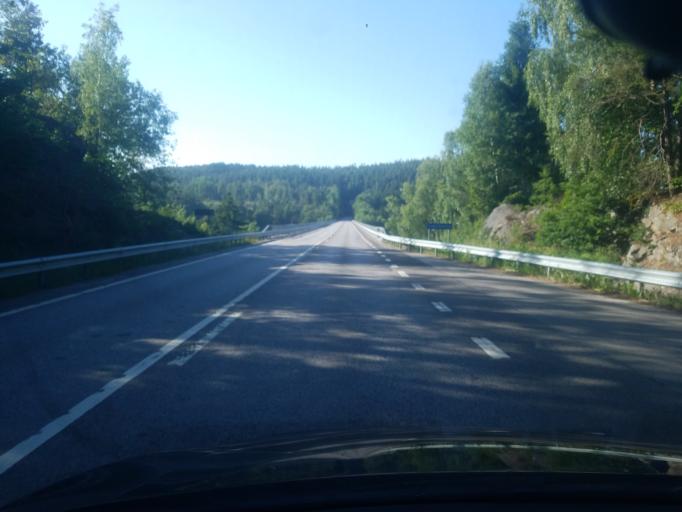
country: SE
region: Vaestra Goetaland
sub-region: Orust
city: Henan
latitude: 58.2929
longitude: 11.7034
